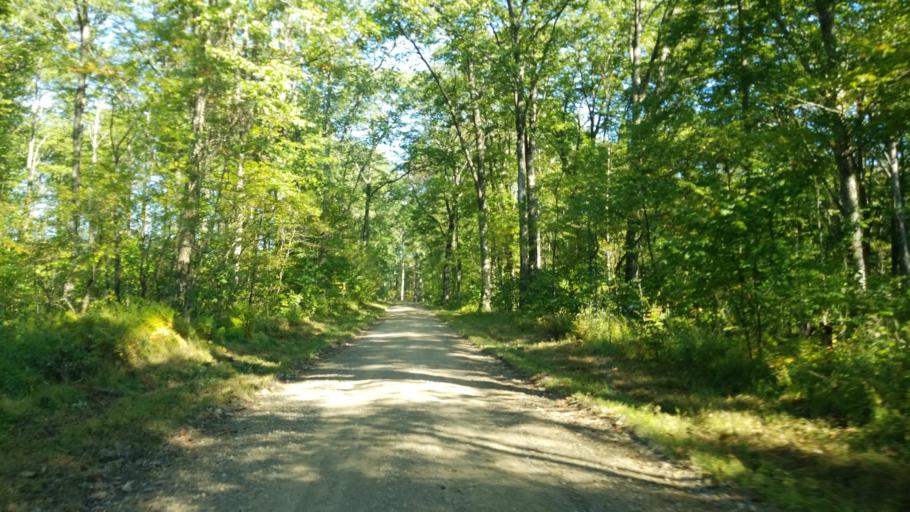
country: US
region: Pennsylvania
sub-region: Clearfield County
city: Curwensville
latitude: 41.1156
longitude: -78.5723
